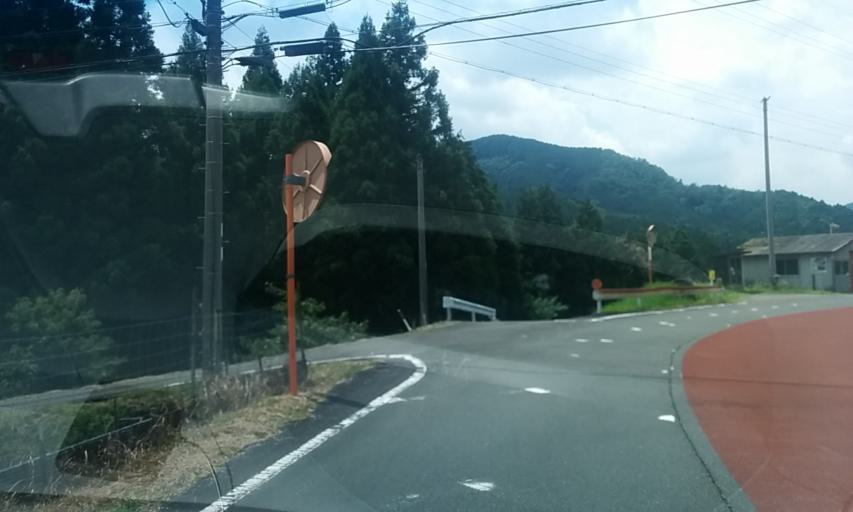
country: JP
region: Kyoto
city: Ayabe
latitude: 35.2122
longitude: 135.2363
